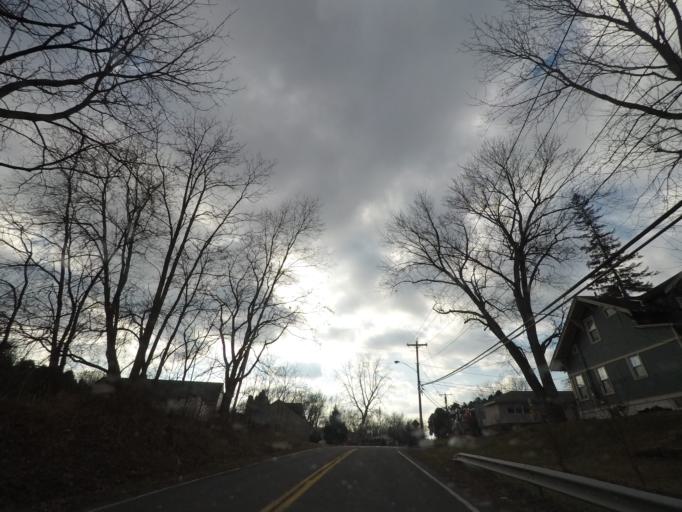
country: US
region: New York
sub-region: Albany County
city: McKownville
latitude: 42.6682
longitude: -73.8274
